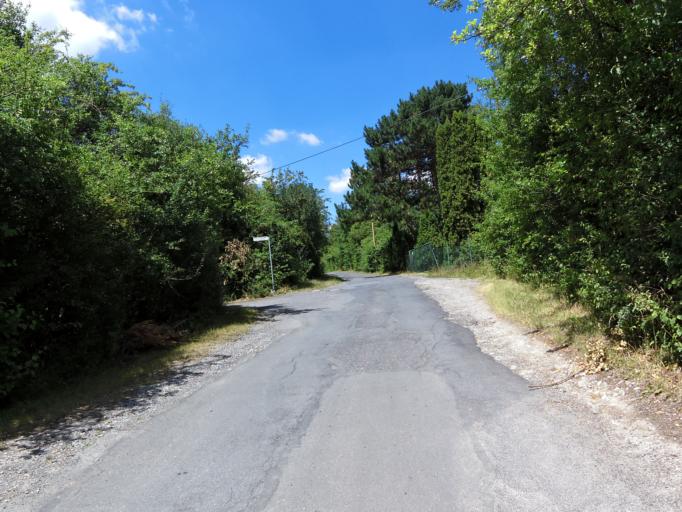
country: DE
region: Bavaria
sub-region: Regierungsbezirk Unterfranken
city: Hochberg
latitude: 49.7723
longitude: 9.8926
